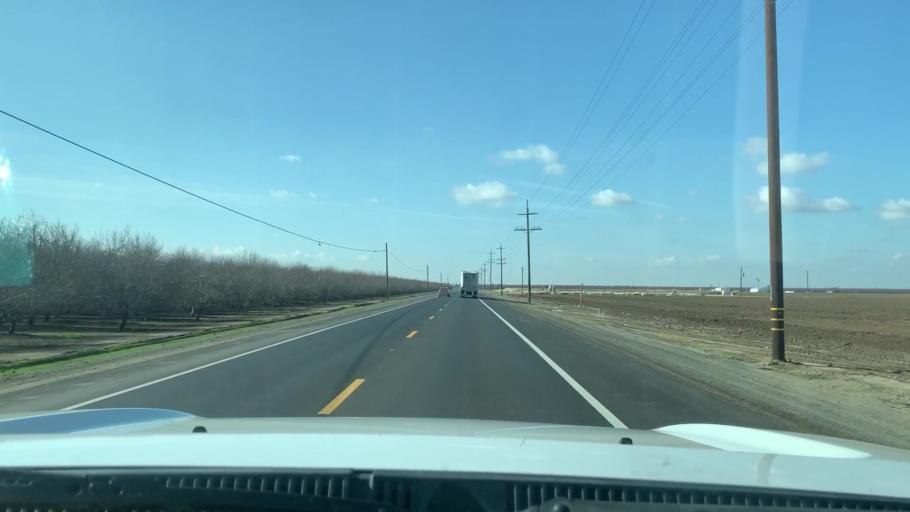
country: US
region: California
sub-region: Kern County
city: Wasco
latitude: 35.6017
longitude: -119.3003
